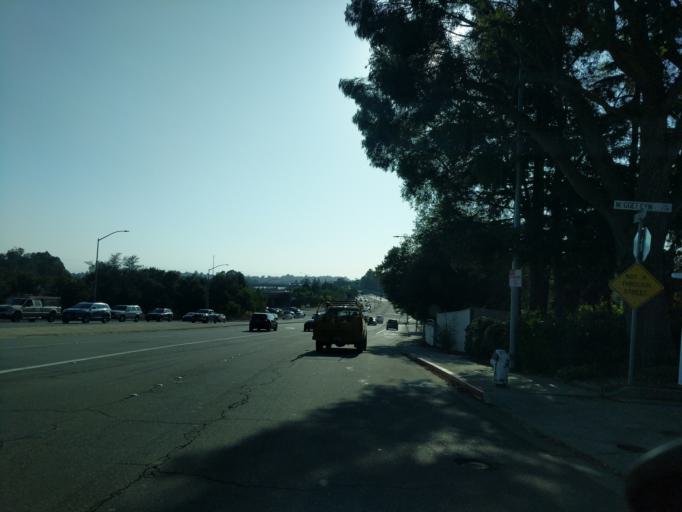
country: US
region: California
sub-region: Alameda County
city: Fairview
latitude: 37.6952
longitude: -122.0552
